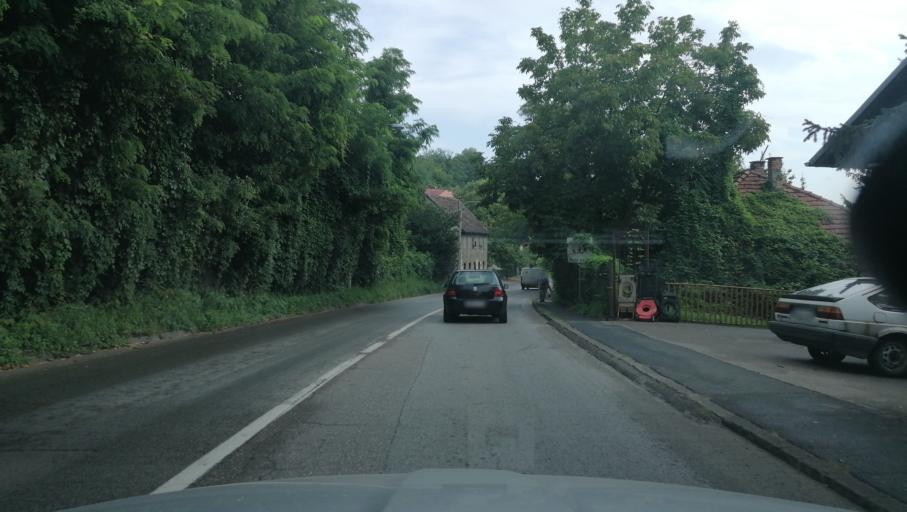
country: BA
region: Republika Srpska
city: Hiseti
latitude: 44.7645
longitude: 17.1764
